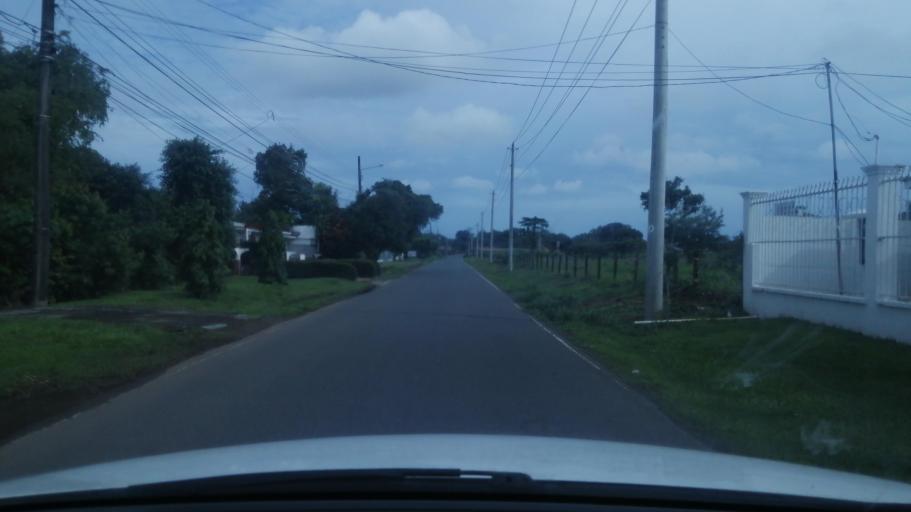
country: PA
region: Chiriqui
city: David
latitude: 8.4071
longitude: -82.4274
